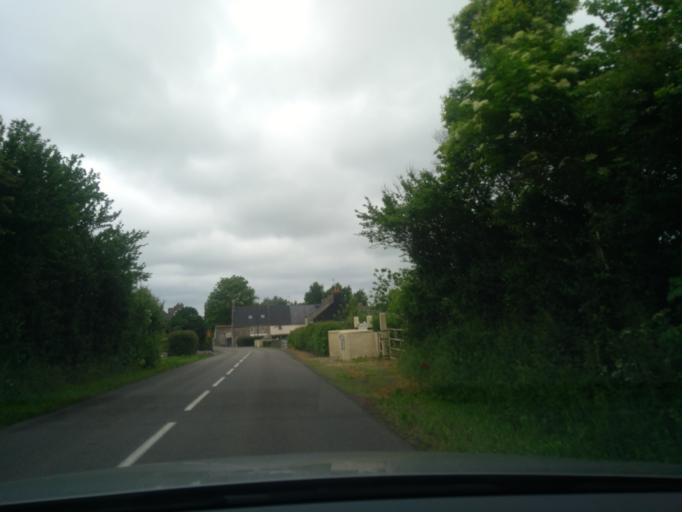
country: FR
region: Lower Normandy
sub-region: Departement de la Manche
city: Sainte-Mere-Eglise
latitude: 49.4461
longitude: -1.2831
